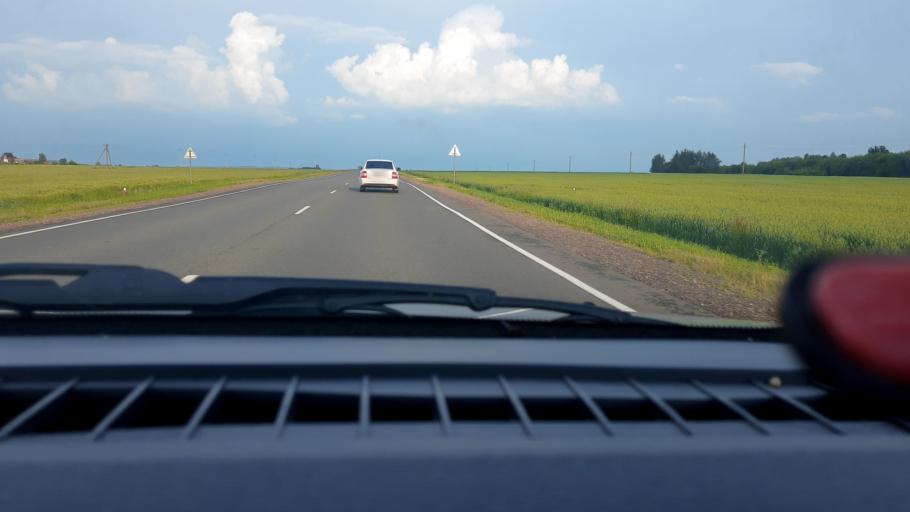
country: RU
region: Nizjnij Novgorod
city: Shatki
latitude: 55.2507
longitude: 43.9906
